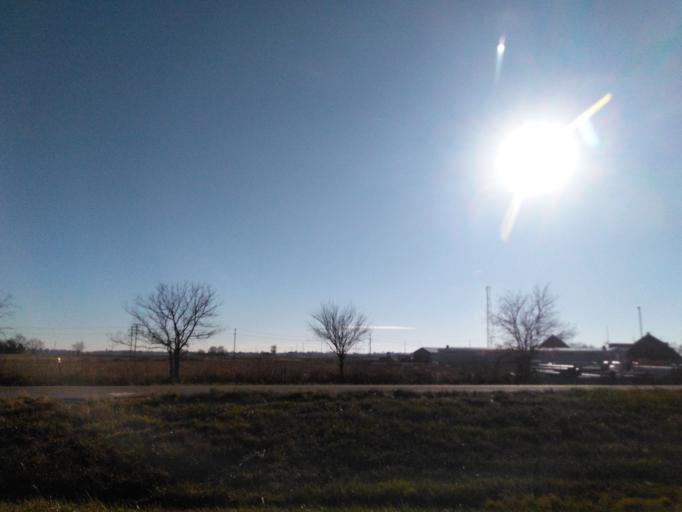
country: US
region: Illinois
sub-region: Madison County
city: Troy
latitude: 38.7200
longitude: -89.9162
